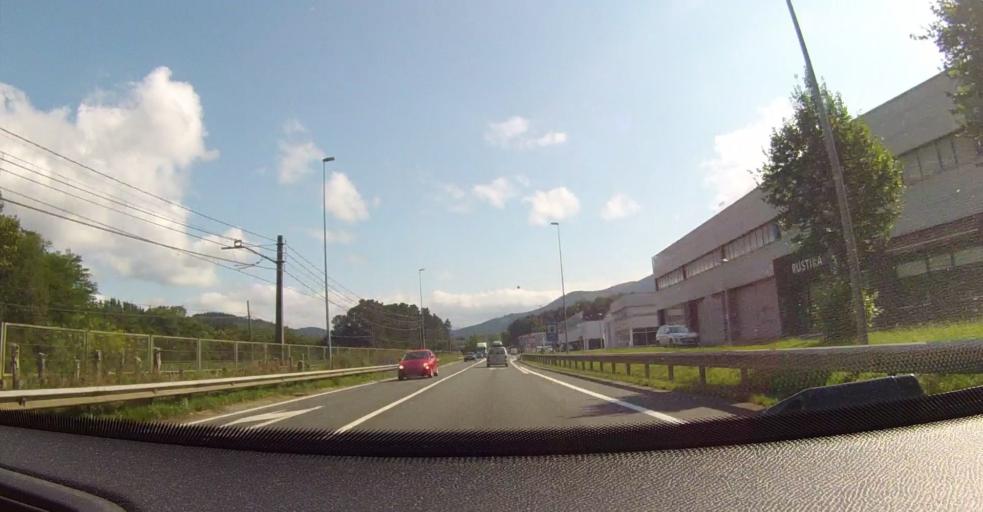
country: ES
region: Basque Country
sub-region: Bizkaia
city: Muxika
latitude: 43.2980
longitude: -2.6862
